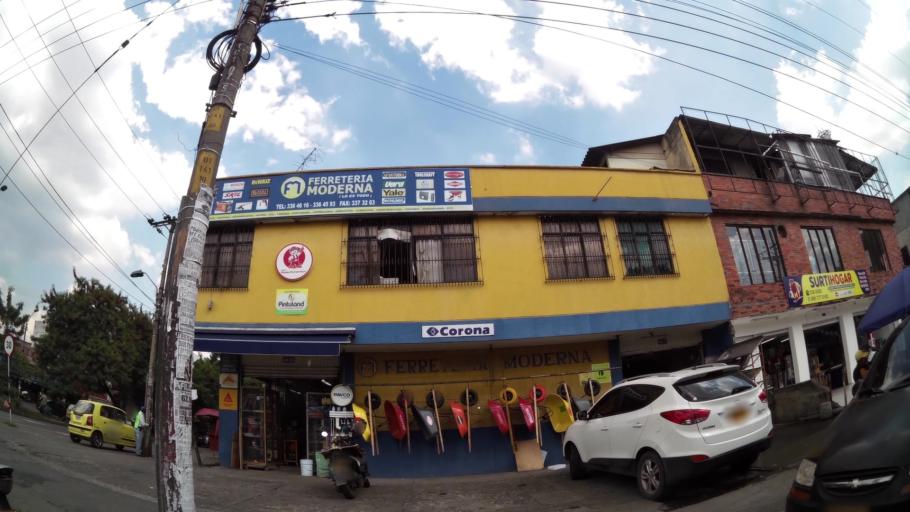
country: CO
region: Valle del Cauca
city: Cali
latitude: 3.4130
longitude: -76.5287
